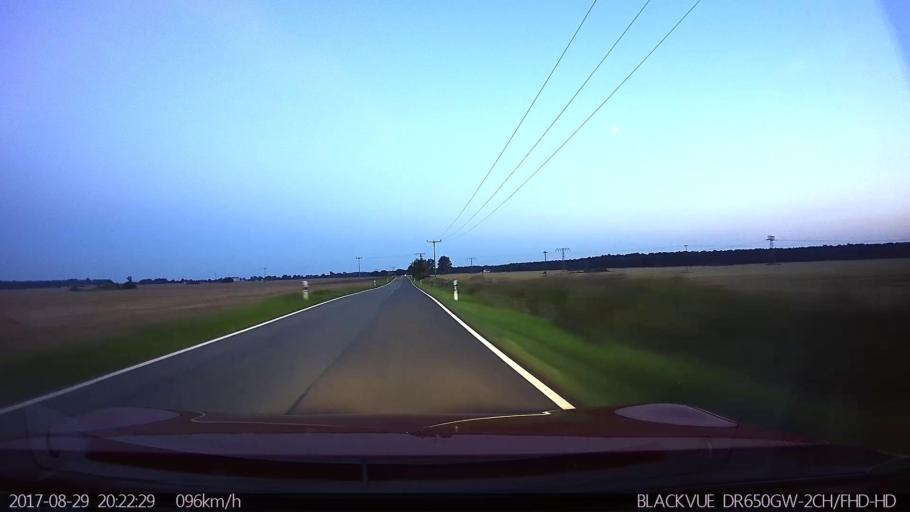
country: DE
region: Mecklenburg-Vorpommern
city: Velgast
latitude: 54.2380
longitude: 12.8243
